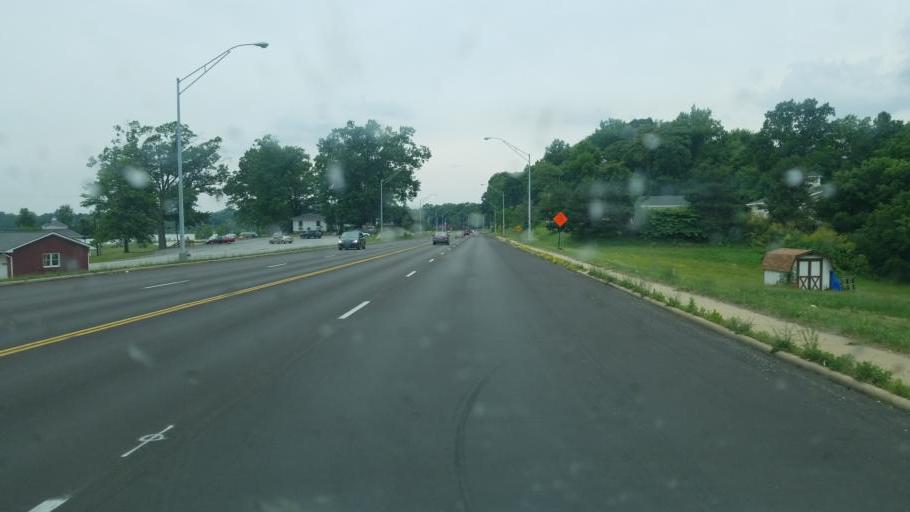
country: US
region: Ohio
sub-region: Summit County
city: Sawyerwood
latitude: 41.0338
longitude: -81.4371
